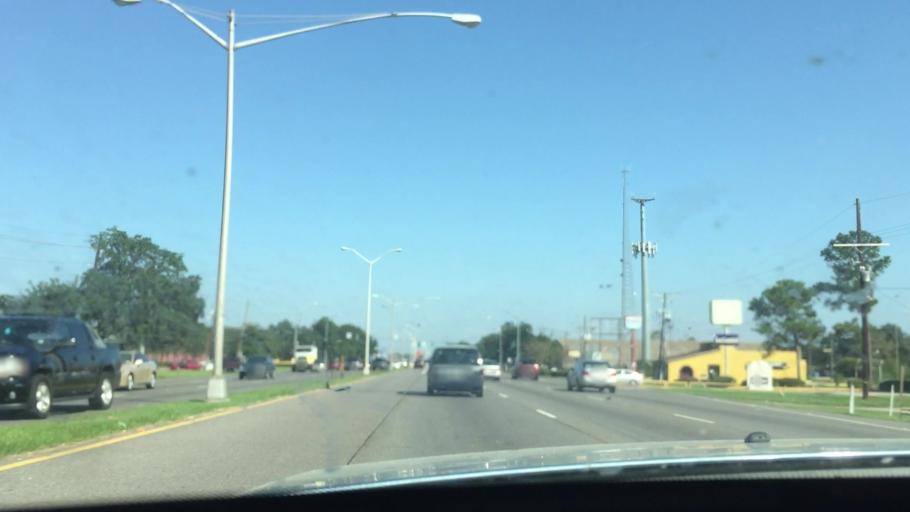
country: US
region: Louisiana
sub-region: East Baton Rouge Parish
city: Baton Rouge
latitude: 30.4516
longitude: -91.1160
